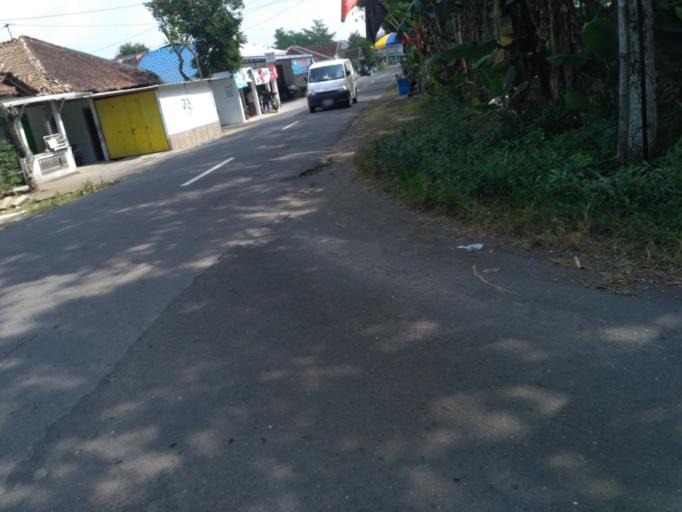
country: ID
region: Daerah Istimewa Yogyakarta
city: Depok
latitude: -7.7190
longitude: 110.4236
